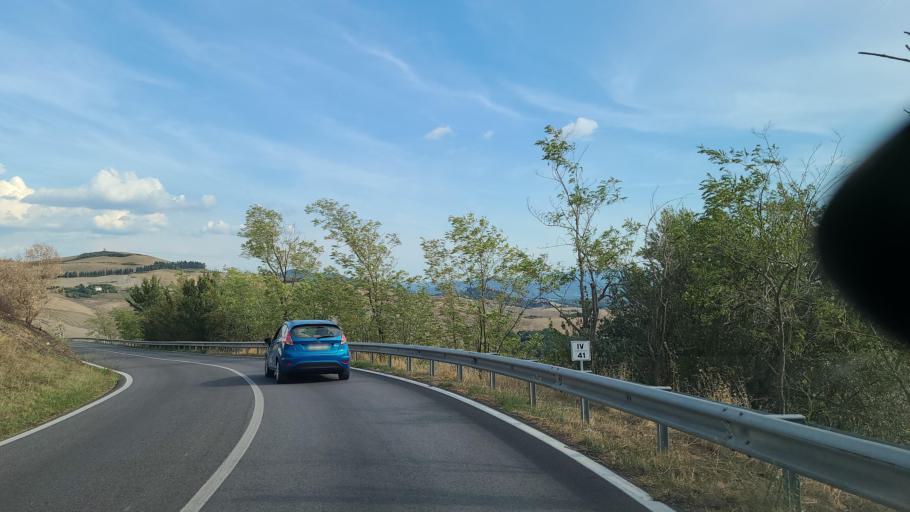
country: IT
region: Tuscany
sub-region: Province of Pisa
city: Volterra
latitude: 43.3938
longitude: 10.8892
